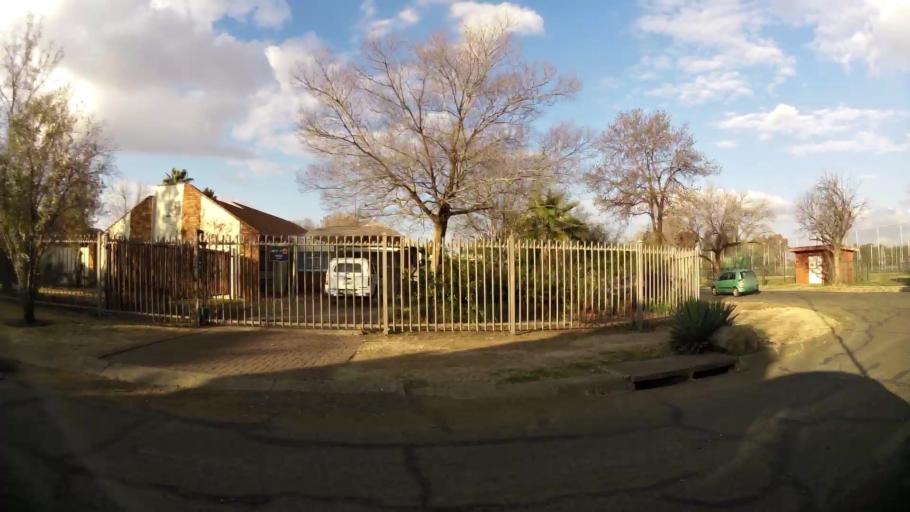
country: ZA
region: Orange Free State
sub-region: Mangaung Metropolitan Municipality
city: Bloemfontein
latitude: -29.1467
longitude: 26.1842
